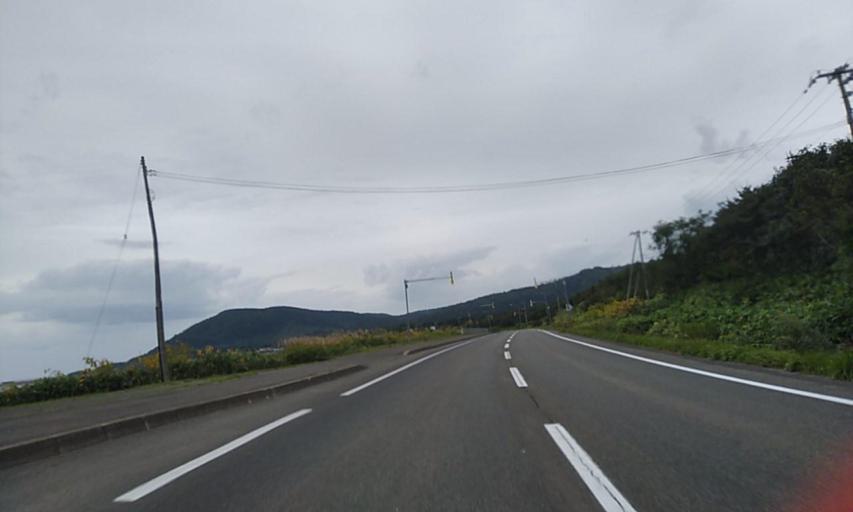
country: JP
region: Hokkaido
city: Nayoro
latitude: 45.0418
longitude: 142.5062
